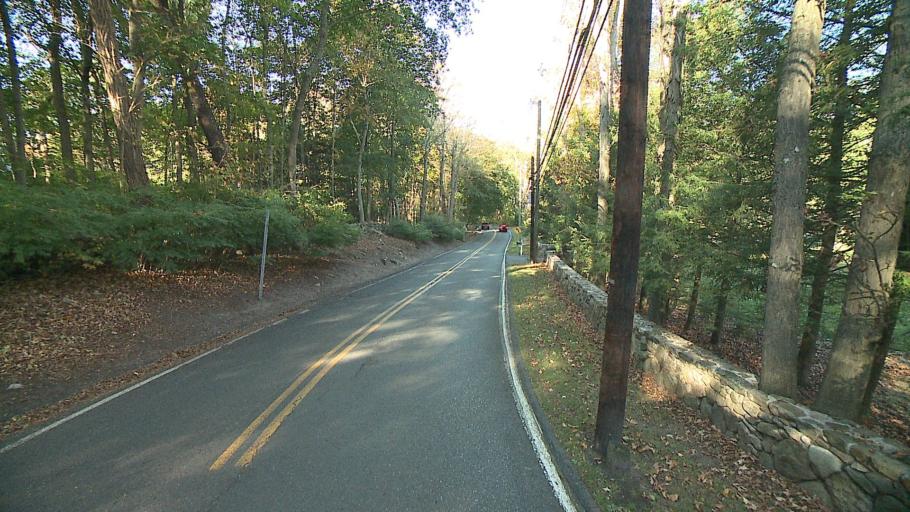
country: US
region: Connecticut
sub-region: Fairfield County
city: Wilton
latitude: 41.1997
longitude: -73.3845
